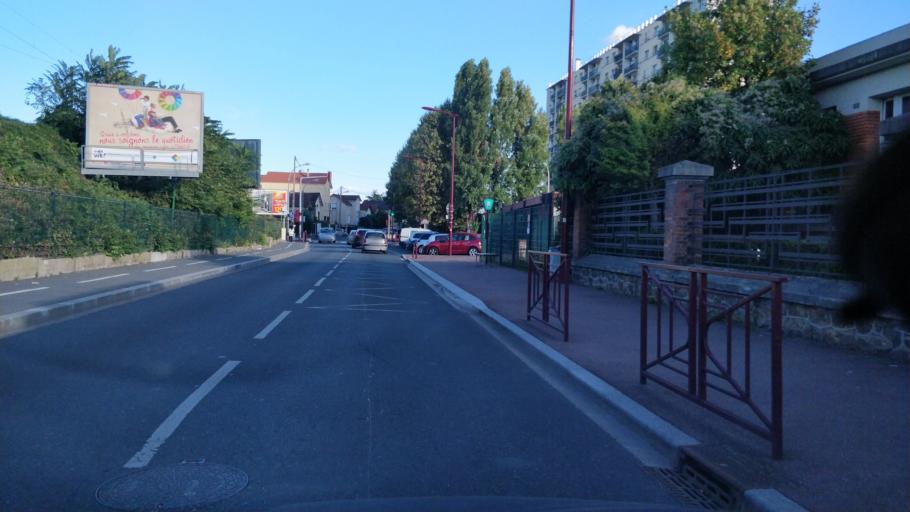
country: FR
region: Ile-de-France
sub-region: Departement de Seine-Saint-Denis
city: Bondy
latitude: 48.8922
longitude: 2.4880
